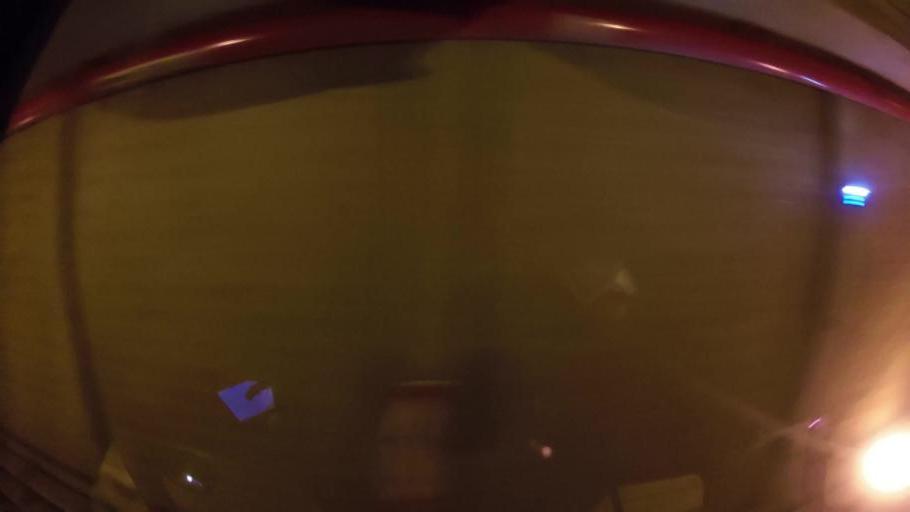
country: CO
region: Bolivar
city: Cartagena
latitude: 10.4477
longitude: -75.5211
